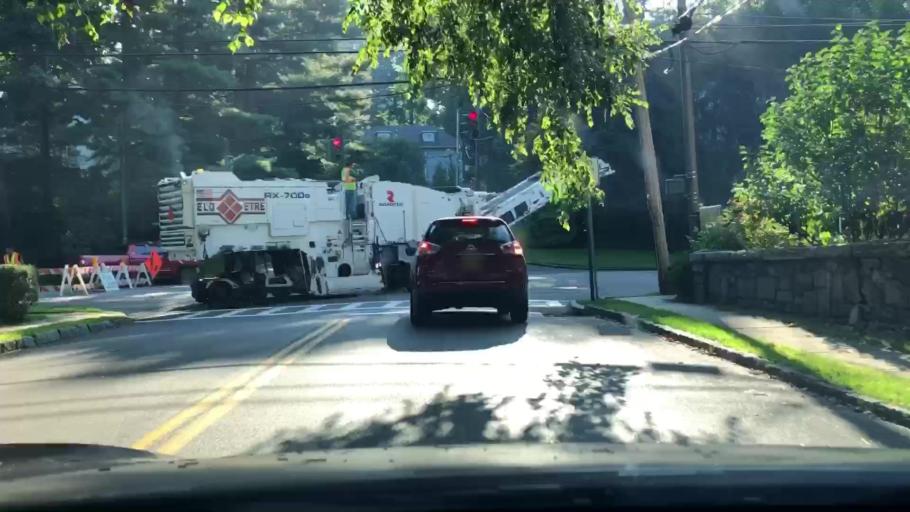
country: US
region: New York
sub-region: Westchester County
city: Bronxville
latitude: 40.9415
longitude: -73.8267
